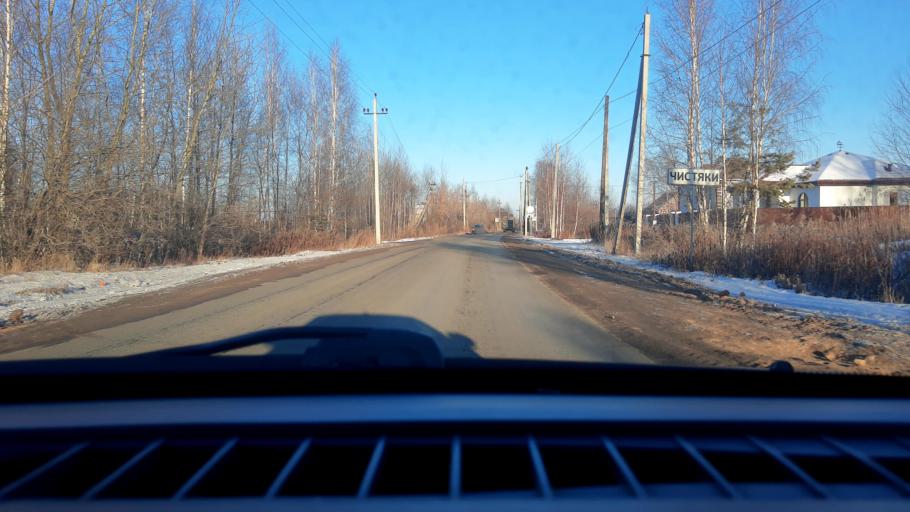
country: RU
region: Nizjnij Novgorod
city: Bor
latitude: 56.3775
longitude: 44.0812
